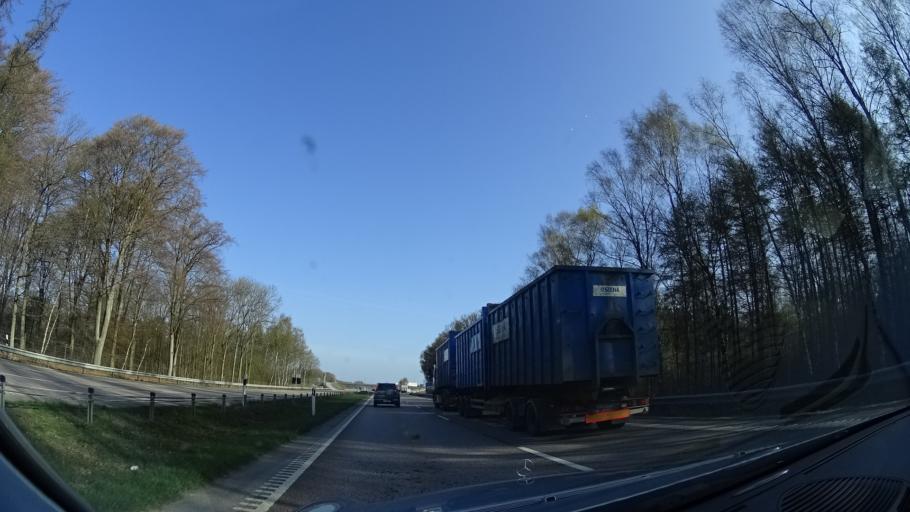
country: SE
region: Skane
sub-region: Helsingborg
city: Odakra
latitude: 56.0605
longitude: 12.7826
